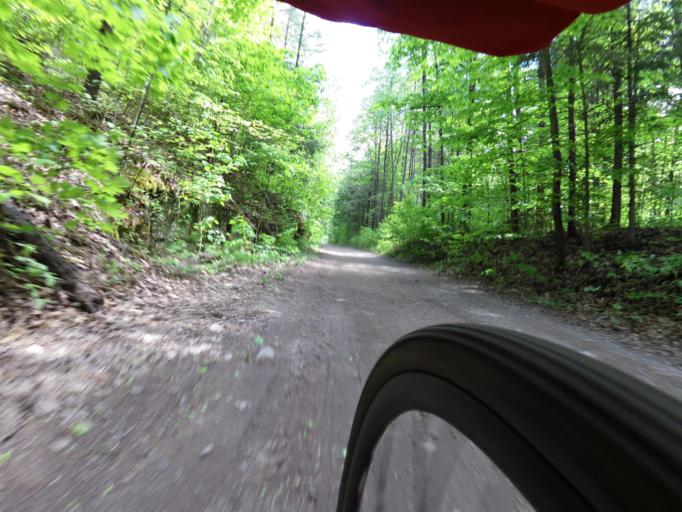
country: CA
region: Ontario
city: Renfrew
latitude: 45.2087
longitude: -76.6914
